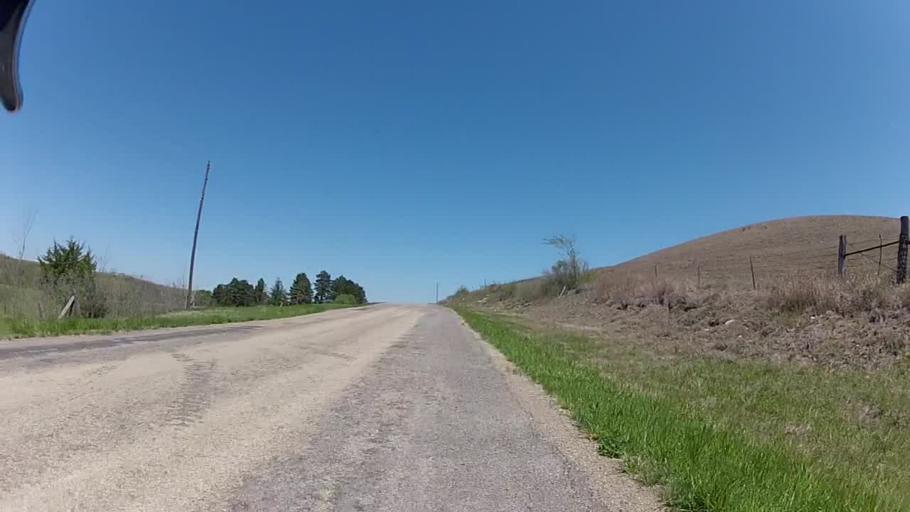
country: US
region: Kansas
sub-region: Riley County
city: Ogden
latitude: 38.9790
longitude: -96.5881
